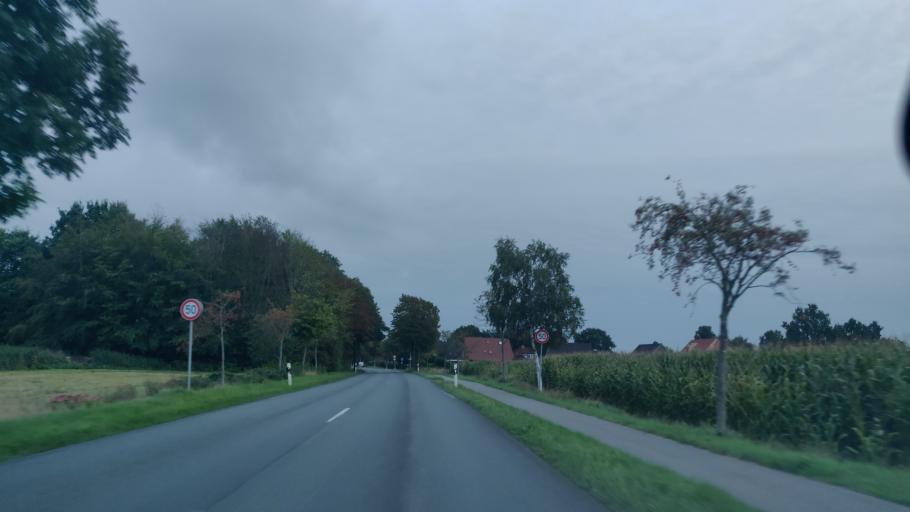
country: DE
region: Lower Saxony
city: Aurich
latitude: 53.4845
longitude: 7.4468
